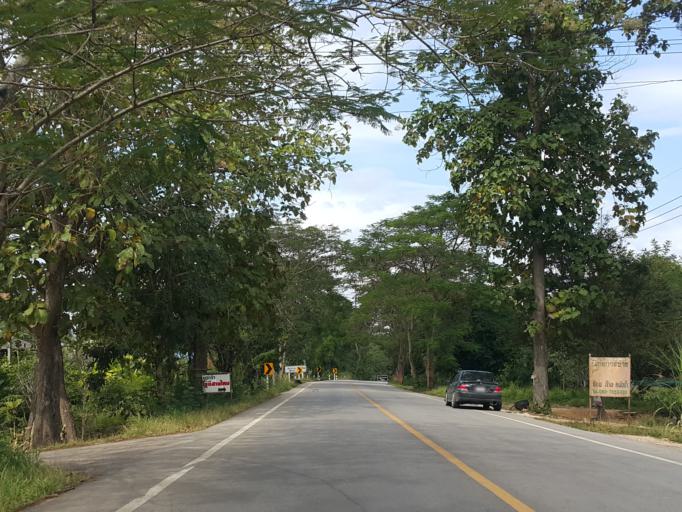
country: TH
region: Lampang
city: Hang Chat
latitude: 18.4225
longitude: 99.4450
